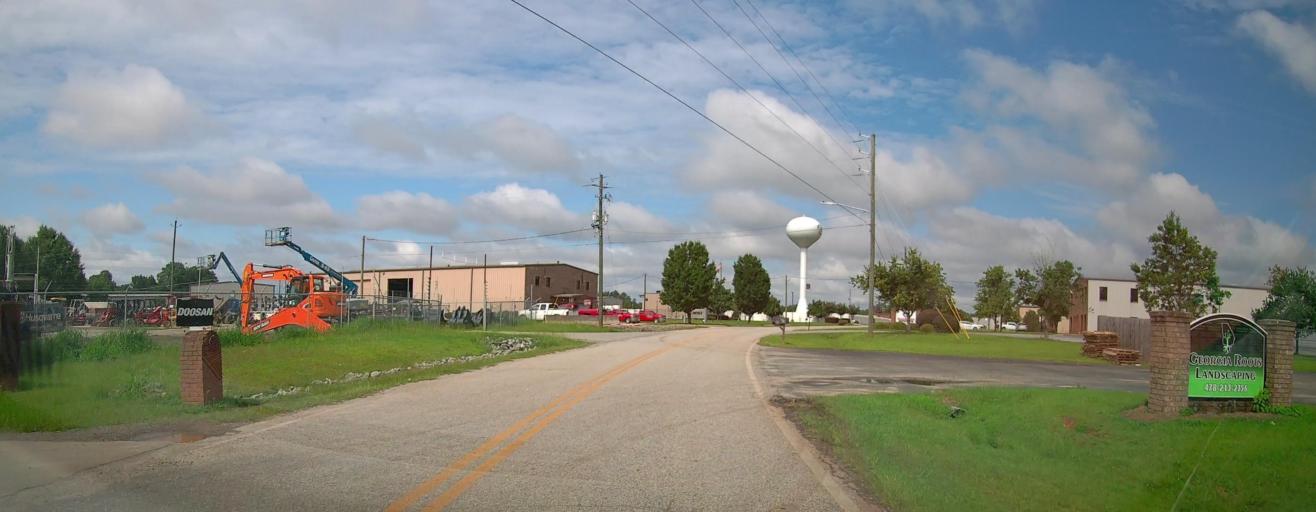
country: US
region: Georgia
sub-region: Peach County
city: Byron
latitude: 32.6474
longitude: -83.7375
